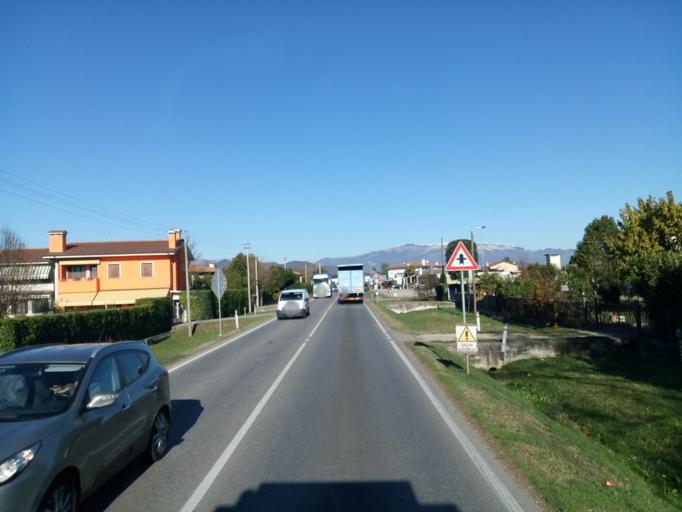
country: IT
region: Veneto
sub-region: Provincia di Treviso
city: Caerano di San Marco
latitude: 45.7646
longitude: 11.9948
